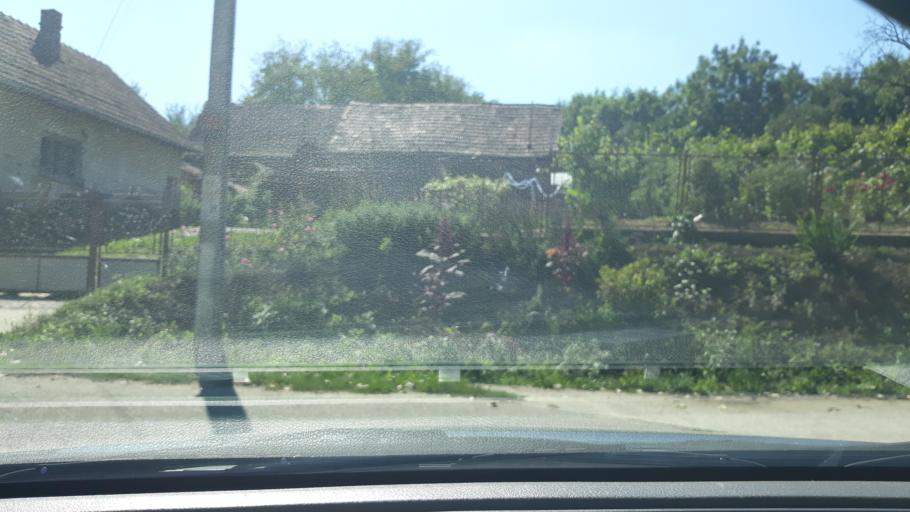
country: RO
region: Salaj
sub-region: Comuna Dobrin
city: Dobrin
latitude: 47.2930
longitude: 23.0938
